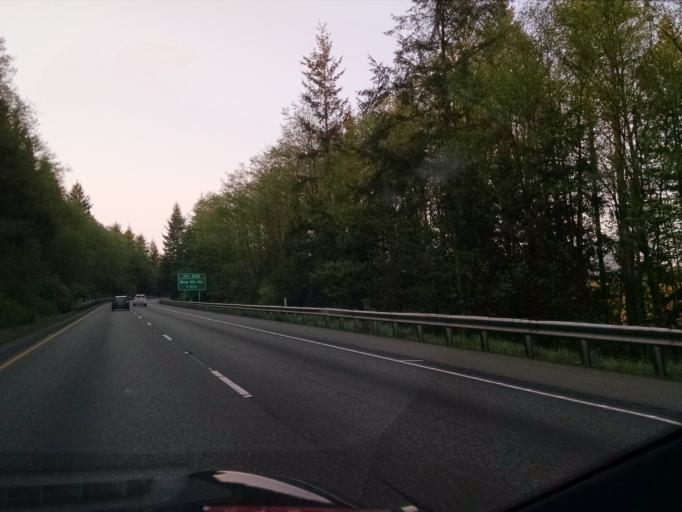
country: US
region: Washington
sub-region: Skagit County
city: Burlington
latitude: 48.5405
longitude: -122.3519
